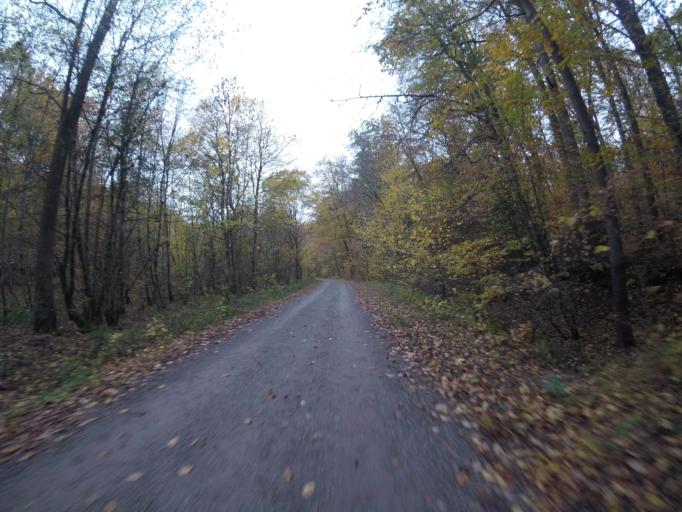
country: DE
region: Baden-Wuerttemberg
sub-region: Regierungsbezirk Stuttgart
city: Kirchberg an der Murr
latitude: 48.9783
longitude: 9.3283
